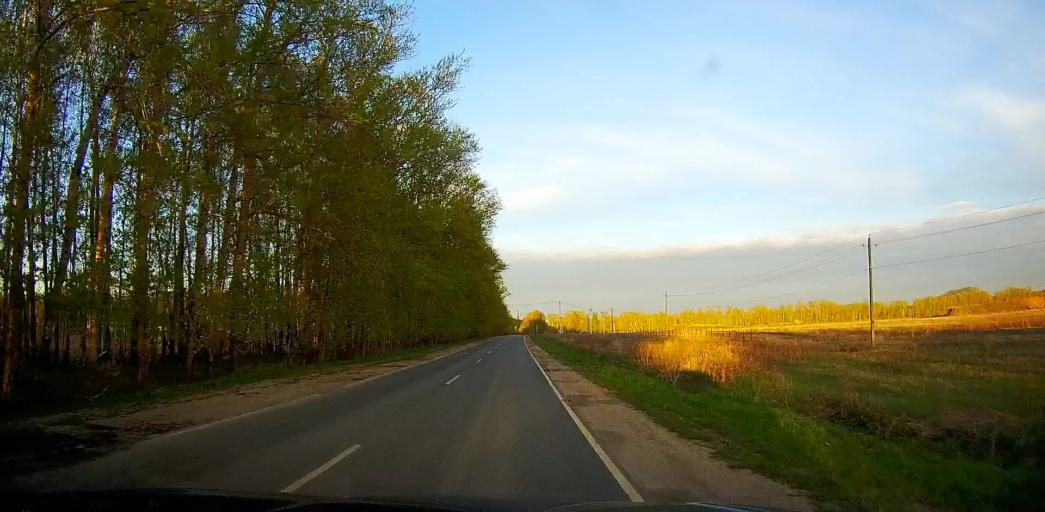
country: RU
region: Moskovskaya
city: Peski
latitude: 55.2098
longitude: 38.7027
